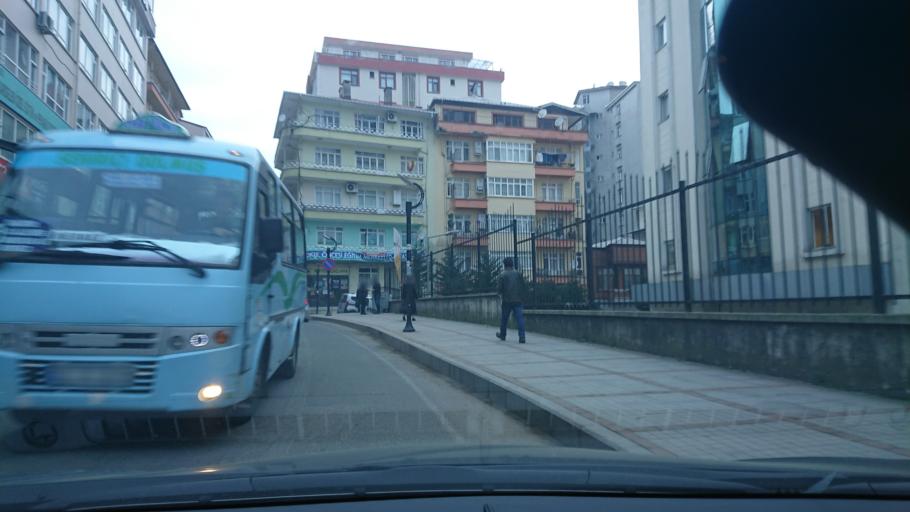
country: TR
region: Rize
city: Rize
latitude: 41.0283
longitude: 40.5139
